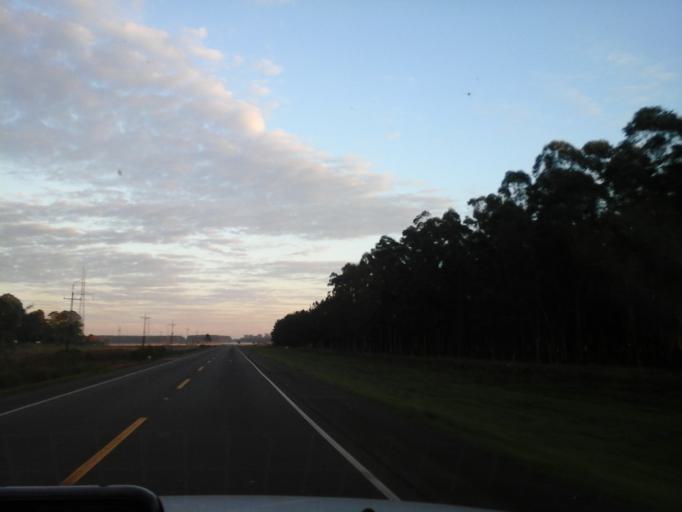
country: PY
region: Itapua
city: General Delgado
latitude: -27.0713
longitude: -56.6065
